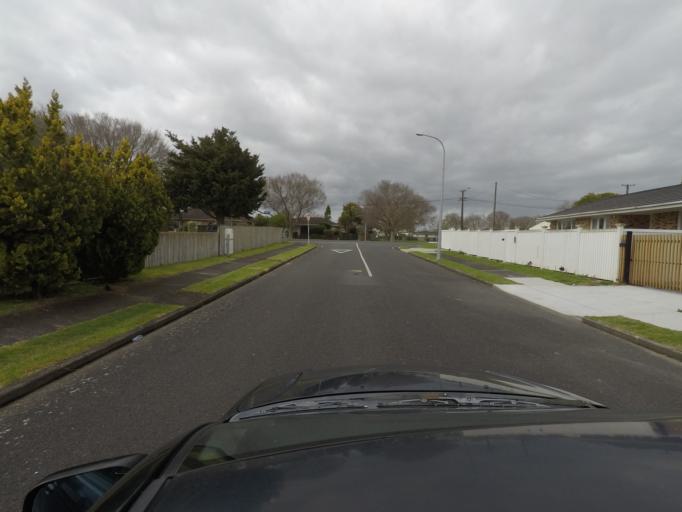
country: NZ
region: Auckland
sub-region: Auckland
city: Tamaki
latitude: -36.9380
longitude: 174.8552
